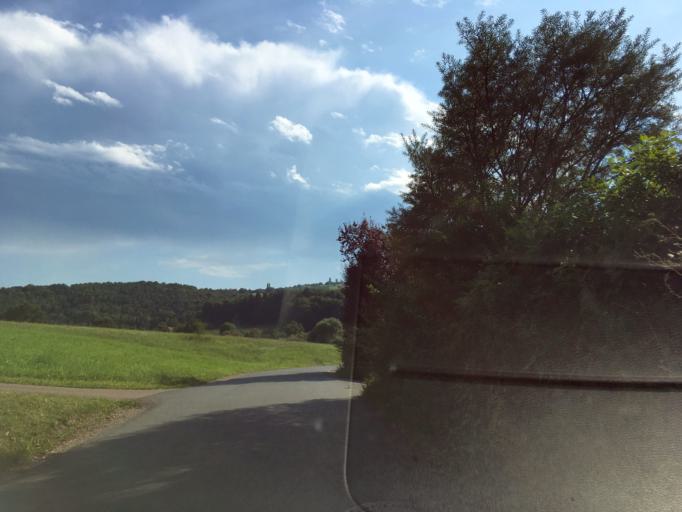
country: AT
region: Styria
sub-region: Politischer Bezirk Leibnitz
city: Sankt Nikolai im Sausal
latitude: 46.8155
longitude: 15.4581
